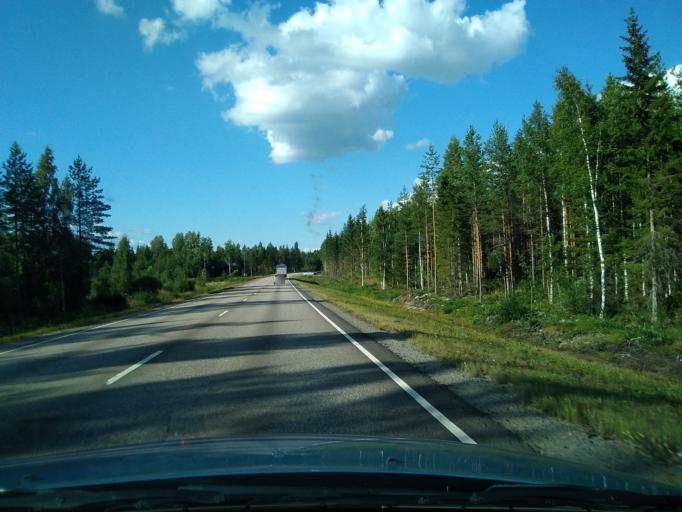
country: FI
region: Central Finland
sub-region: Keuruu
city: Keuruu
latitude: 62.1555
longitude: 24.7503
